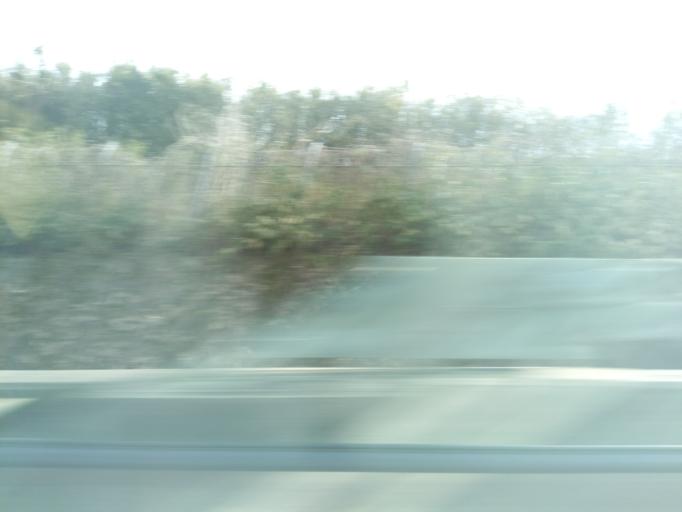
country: JP
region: Miyagi
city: Furukawa
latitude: 38.6642
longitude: 141.0238
